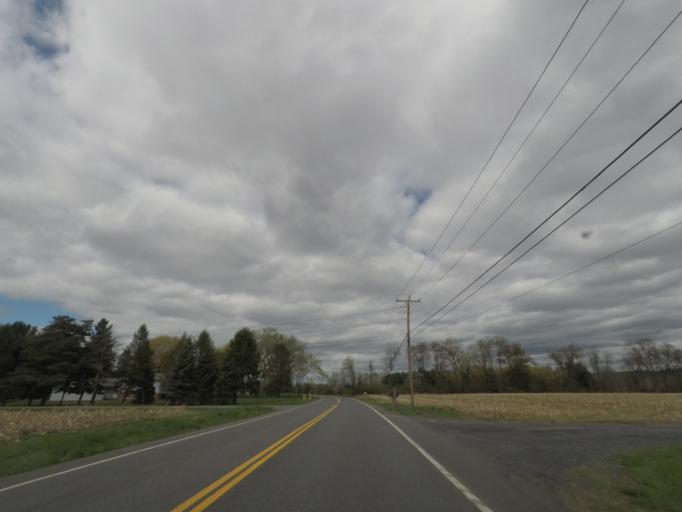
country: US
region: New York
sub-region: Columbia County
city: Philmont
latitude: 42.2888
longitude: -73.6481
